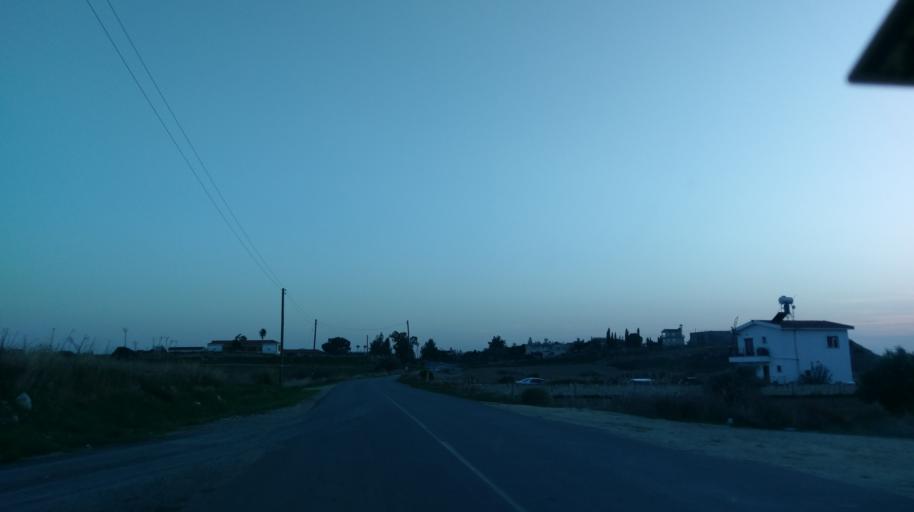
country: CY
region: Ammochostos
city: Trikomo
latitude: 35.2929
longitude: 33.8918
